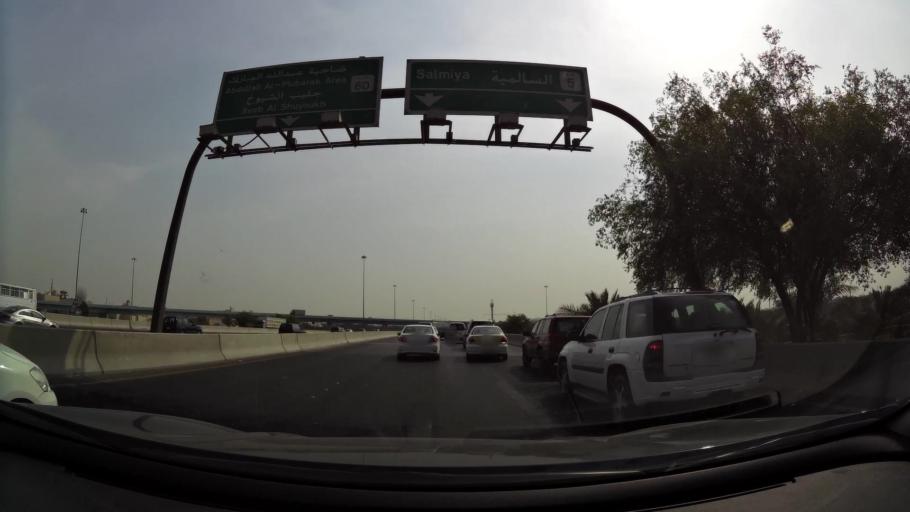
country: KW
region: Al Asimah
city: Ar Rabiyah
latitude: 29.3022
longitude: 47.9450
